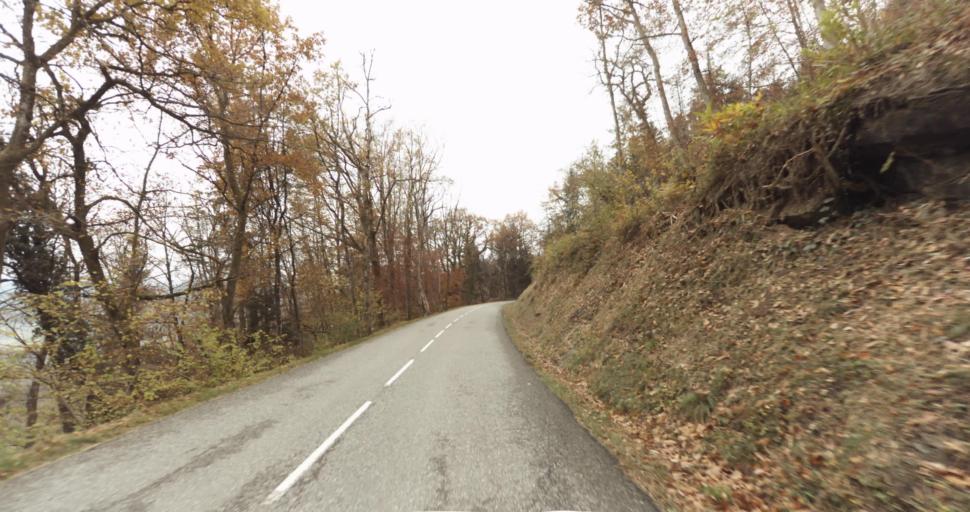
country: FR
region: Rhone-Alpes
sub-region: Departement de la Haute-Savoie
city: Saint-Jorioz
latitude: 45.8097
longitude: 6.1368
